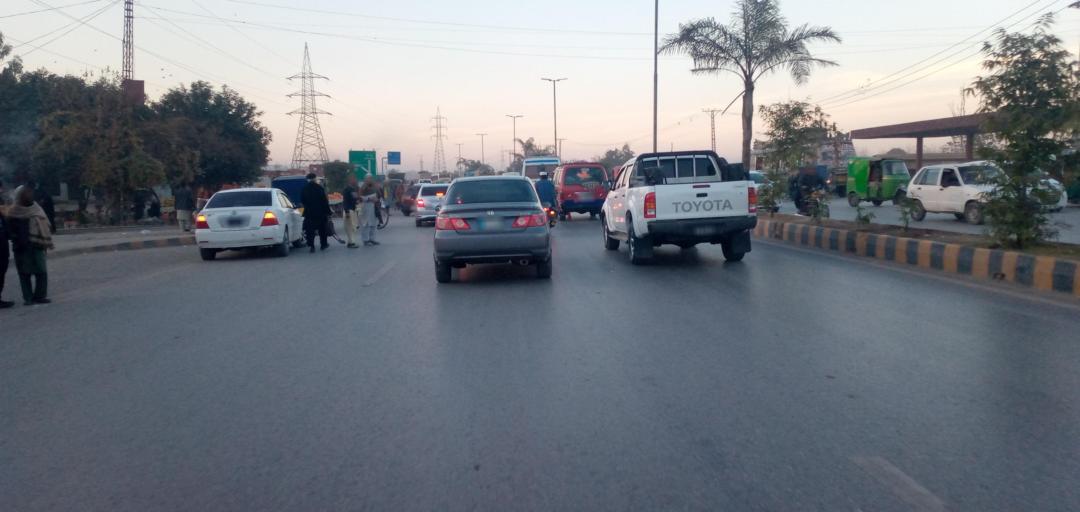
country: PK
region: Khyber Pakhtunkhwa
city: Peshawar
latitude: 34.0242
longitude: 71.6204
